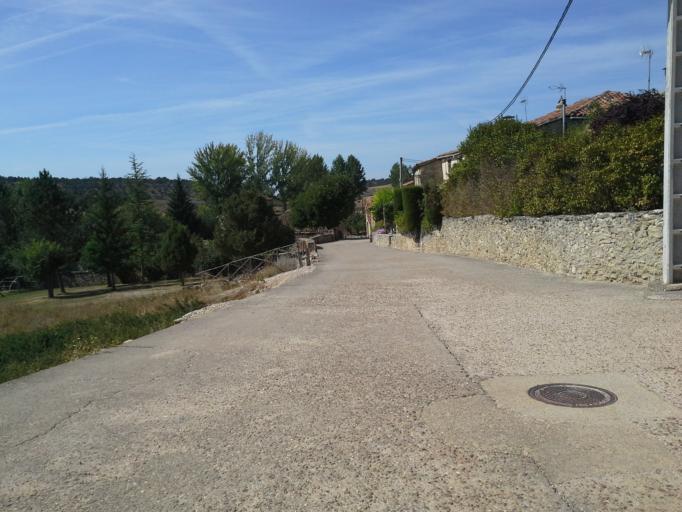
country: ES
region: Castille and Leon
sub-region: Provincia de Soria
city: Abejar
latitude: 41.7380
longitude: -2.7399
